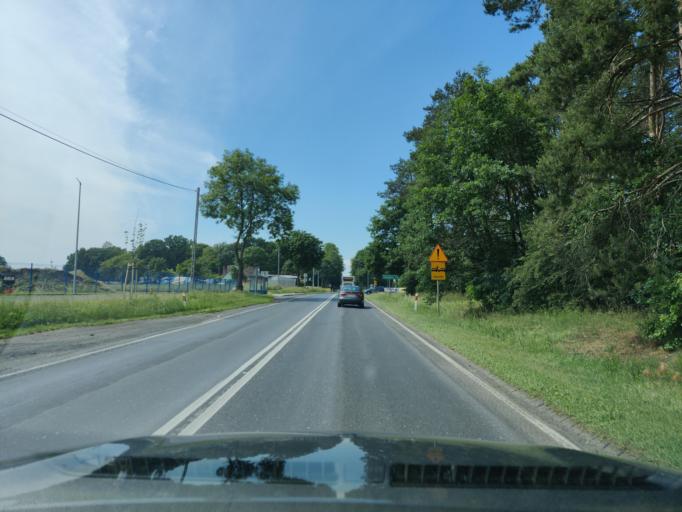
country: PL
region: Greater Poland Voivodeship
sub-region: Powiat grodziski
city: Rakoniewice
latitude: 52.1595
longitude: 16.3048
